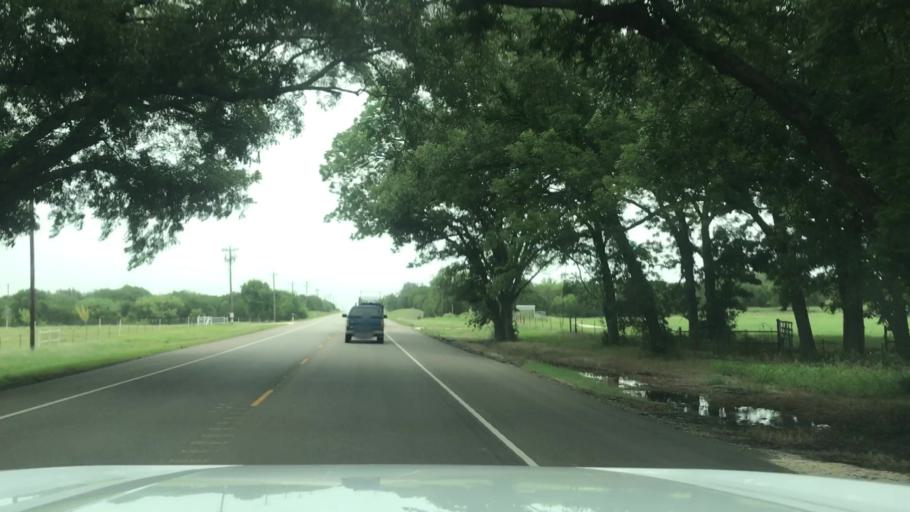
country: US
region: Texas
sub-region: Bosque County
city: Meridian
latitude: 31.9363
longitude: -97.7032
